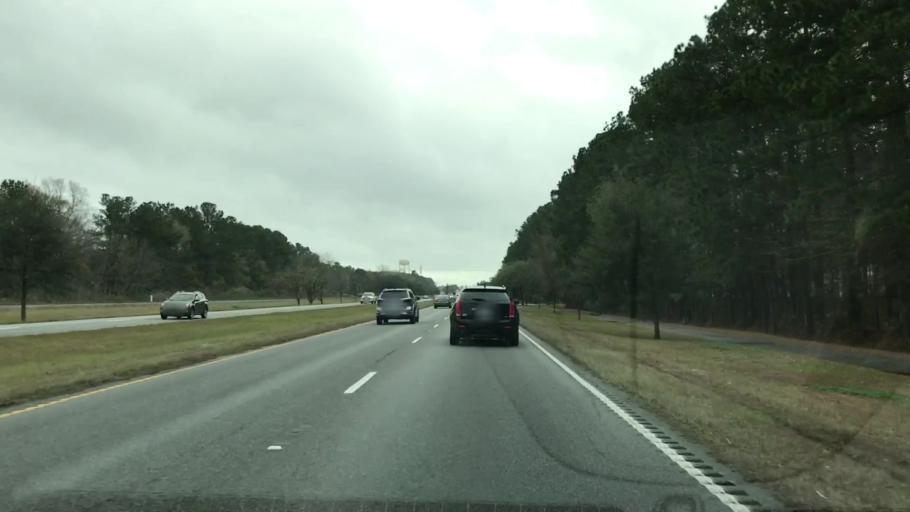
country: US
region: South Carolina
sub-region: Berkeley County
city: Goose Creek
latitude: 33.0151
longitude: -80.0366
